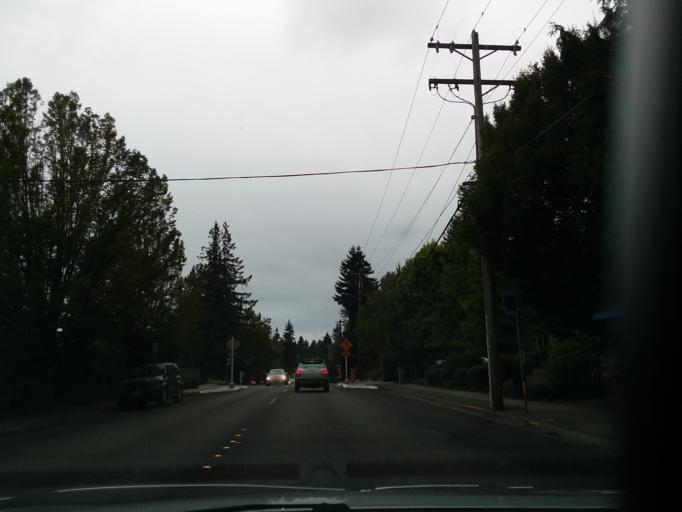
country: US
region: Washington
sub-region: Snohomish County
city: Alderwood Manor
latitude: 47.8229
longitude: -122.2963
